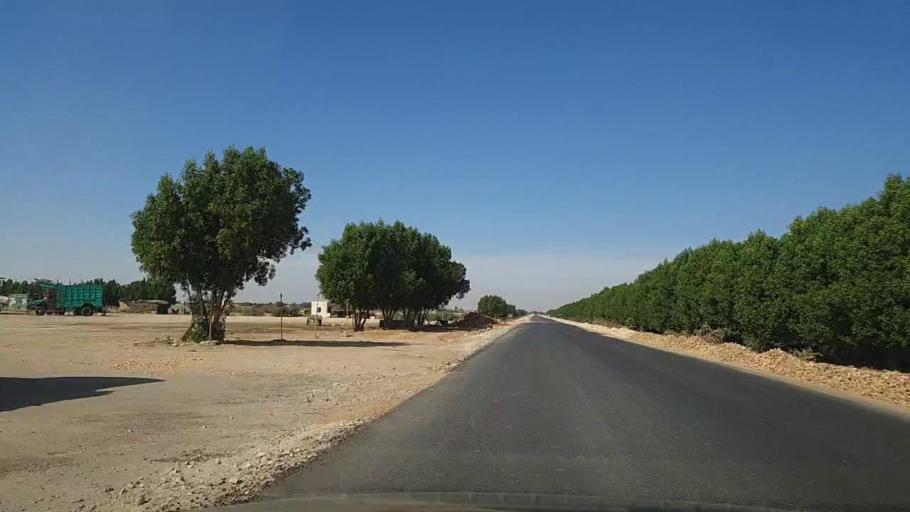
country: PK
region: Sindh
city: Kotri
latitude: 25.2684
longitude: 68.2185
